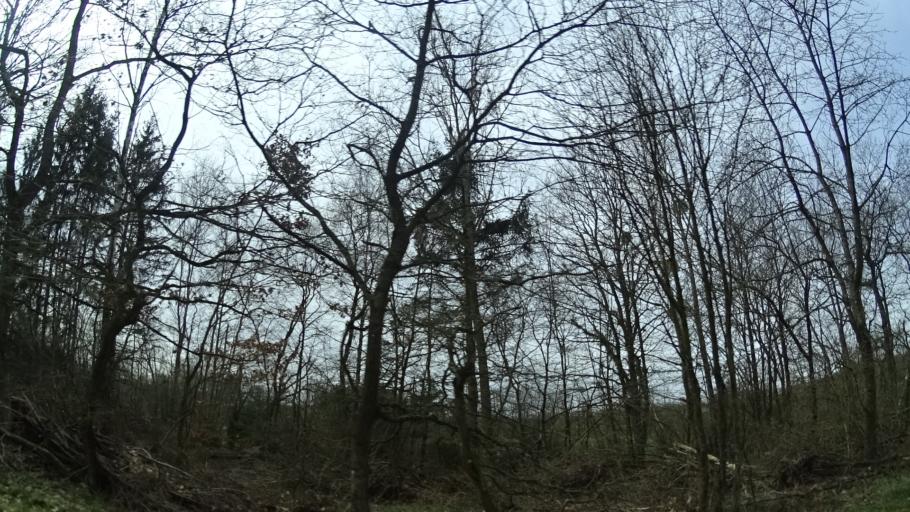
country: DE
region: Rheinland-Pfalz
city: Gebroth
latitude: 49.8874
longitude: 7.6436
